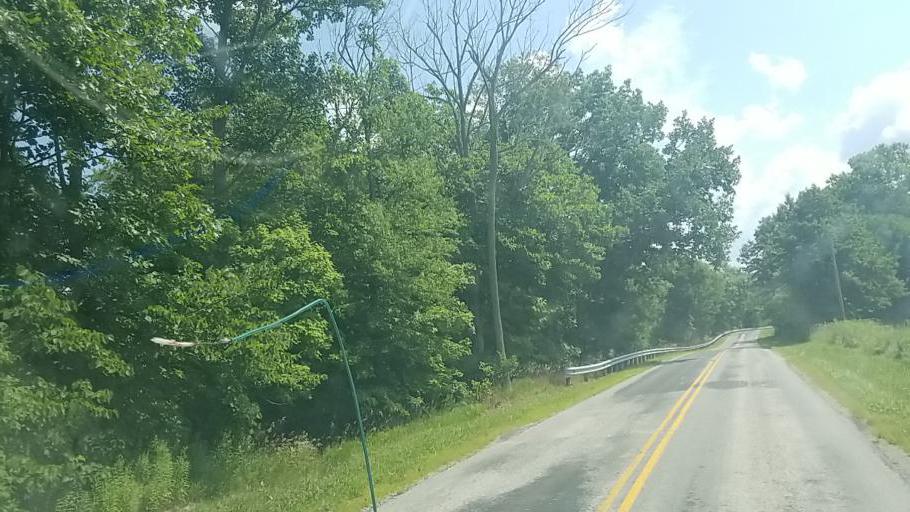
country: US
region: Ohio
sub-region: Wayne County
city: West Salem
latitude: 41.0392
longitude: -82.1316
